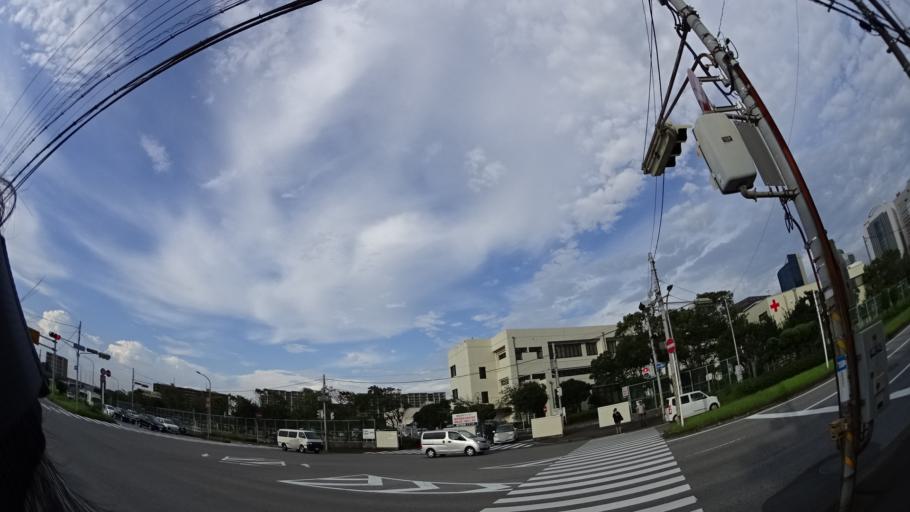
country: JP
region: Chiba
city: Funabashi
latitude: 35.6558
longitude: 140.0332
